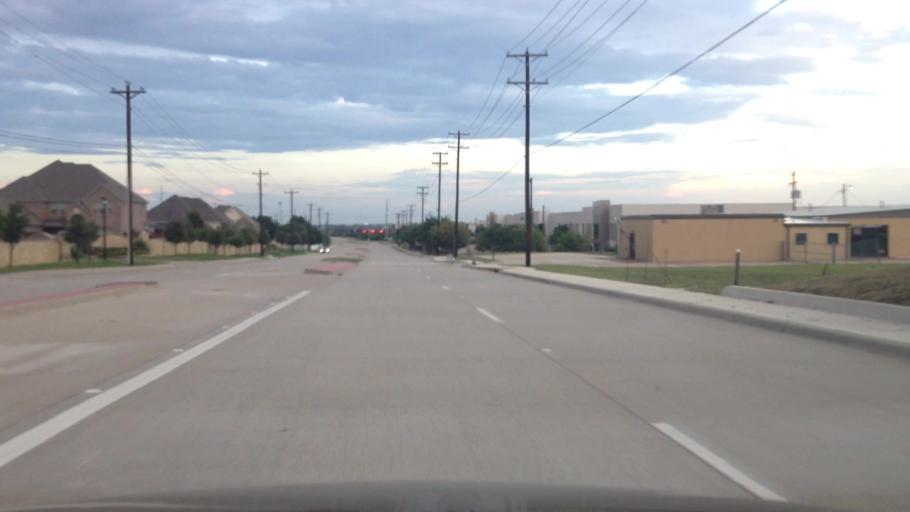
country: US
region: Texas
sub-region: Denton County
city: Flower Mound
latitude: 32.9986
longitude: -97.0508
